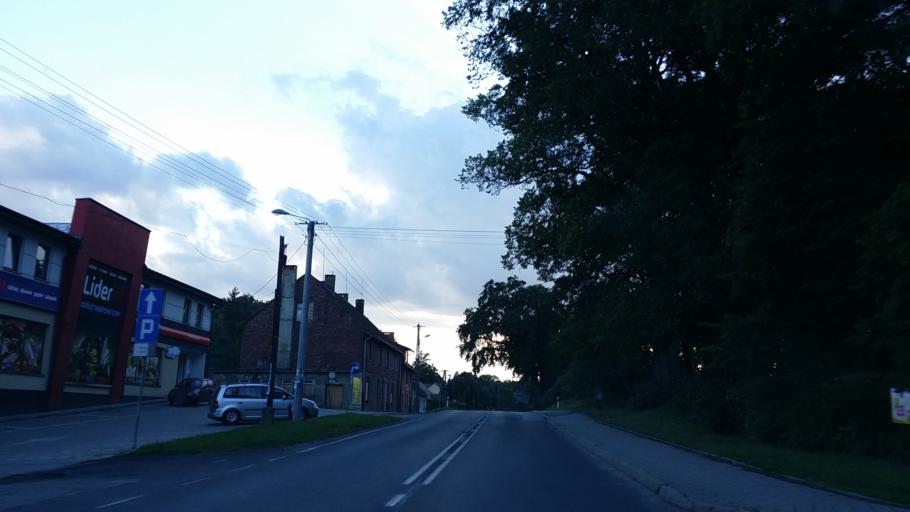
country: PL
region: Lesser Poland Voivodeship
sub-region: Powiat oswiecimski
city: Polanka Wielka
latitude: 49.9851
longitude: 19.3245
